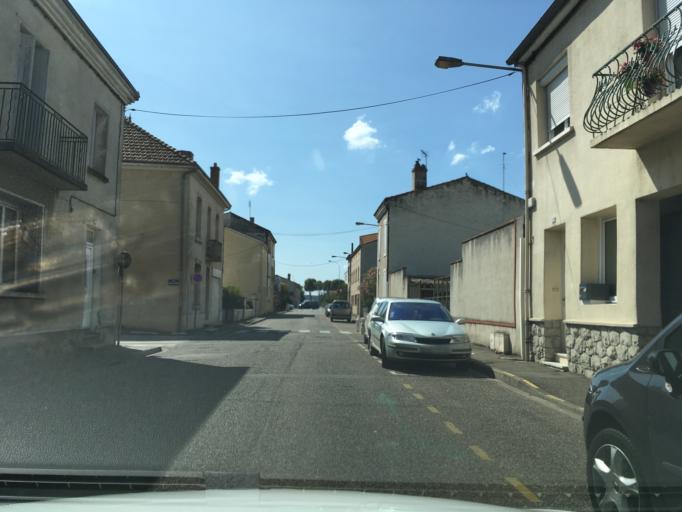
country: FR
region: Aquitaine
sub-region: Departement du Lot-et-Garonne
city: Le Passage
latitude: 44.1946
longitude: 0.6170
